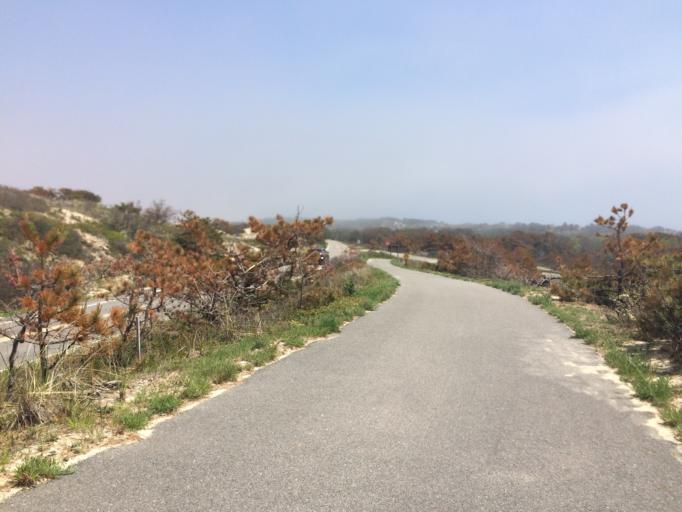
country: US
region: Massachusetts
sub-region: Barnstable County
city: Provincetown
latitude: 42.0776
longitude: -70.2174
